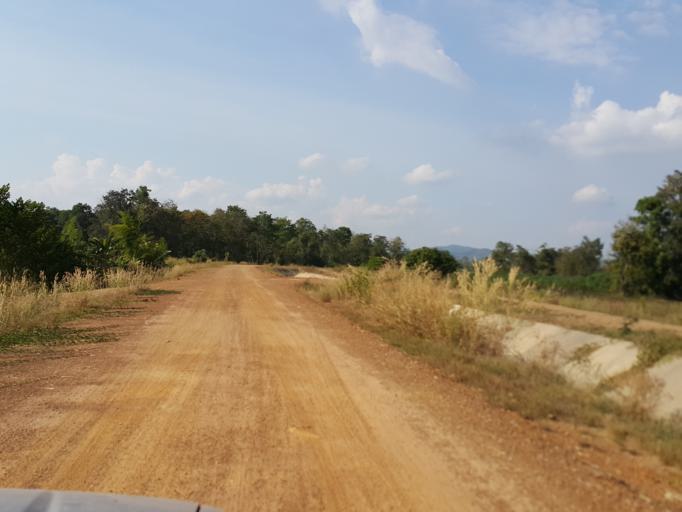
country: TH
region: Sukhothai
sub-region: Amphoe Si Satchanalai
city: Si Satchanalai
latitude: 17.4691
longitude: 99.6637
